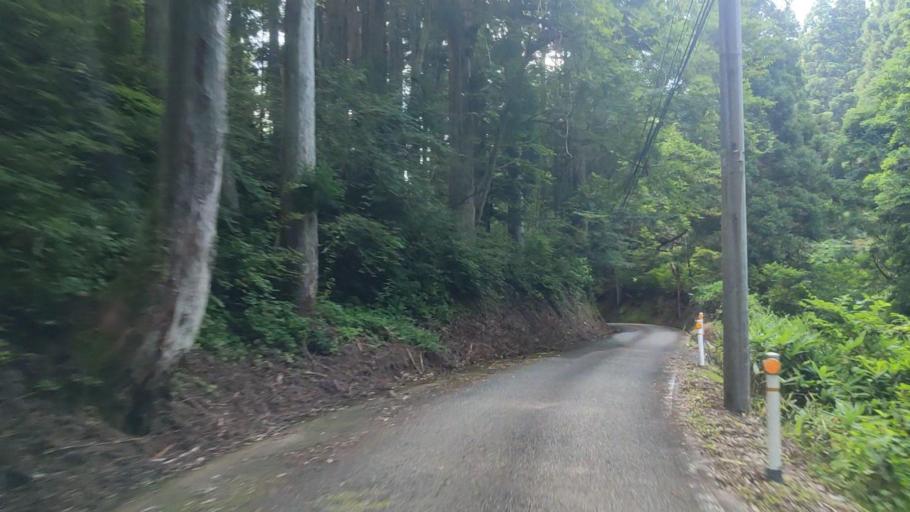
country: JP
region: Ishikawa
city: Komatsu
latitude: 36.2608
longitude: 136.5351
